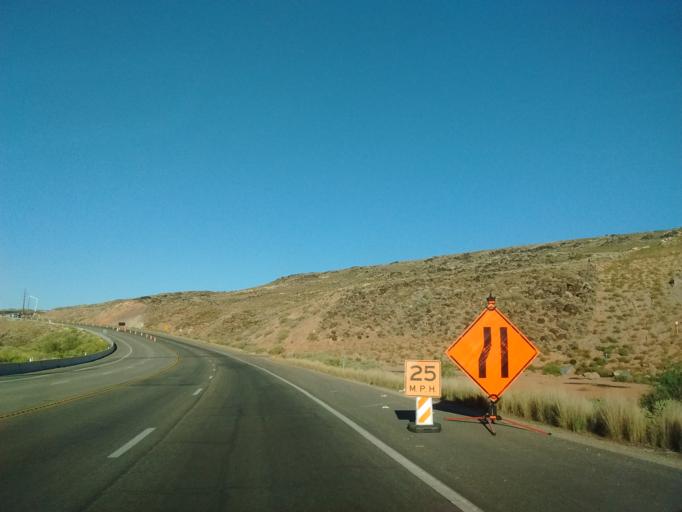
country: US
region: Utah
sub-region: Washington County
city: Washington
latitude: 37.1319
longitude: -113.4816
